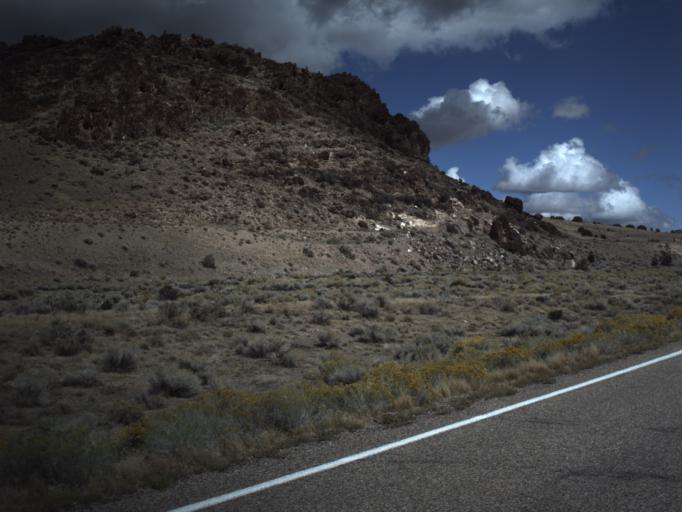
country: US
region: Utah
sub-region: Beaver County
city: Milford
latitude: 38.4345
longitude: -113.2805
